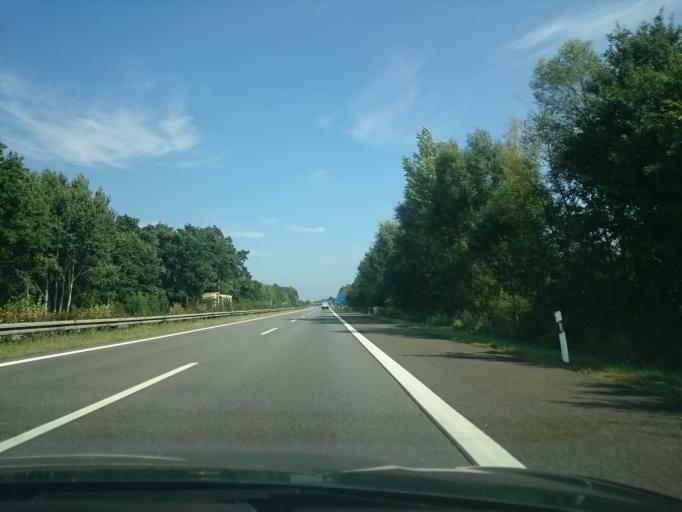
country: DE
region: Brandenburg
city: Lubbenau
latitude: 51.8223
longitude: 13.9023
